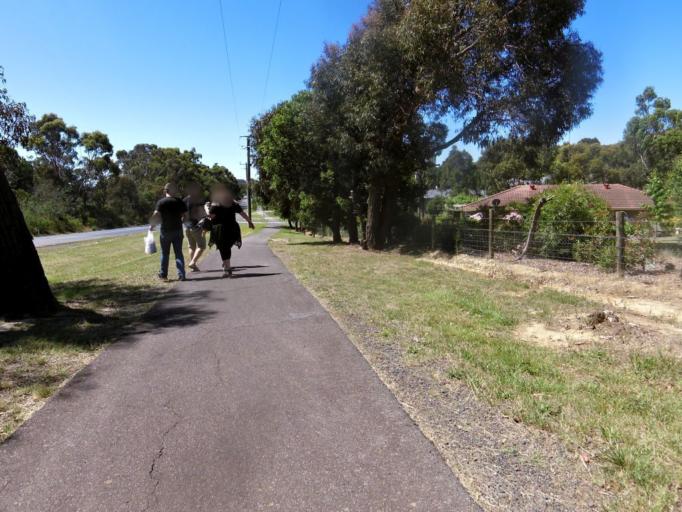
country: AU
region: Victoria
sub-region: Whittlesea
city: Whittlesea
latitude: -37.3652
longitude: 145.0269
